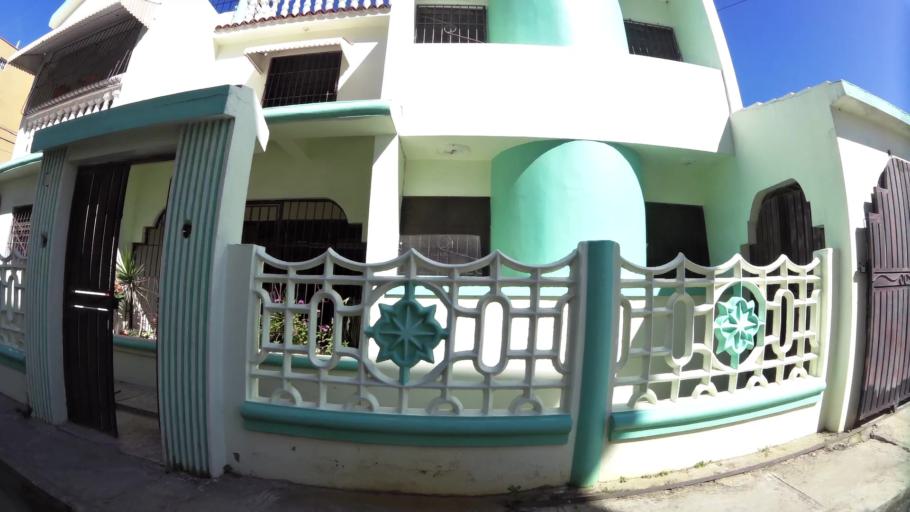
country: DO
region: San Cristobal
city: San Cristobal
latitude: 18.4328
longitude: -70.1204
